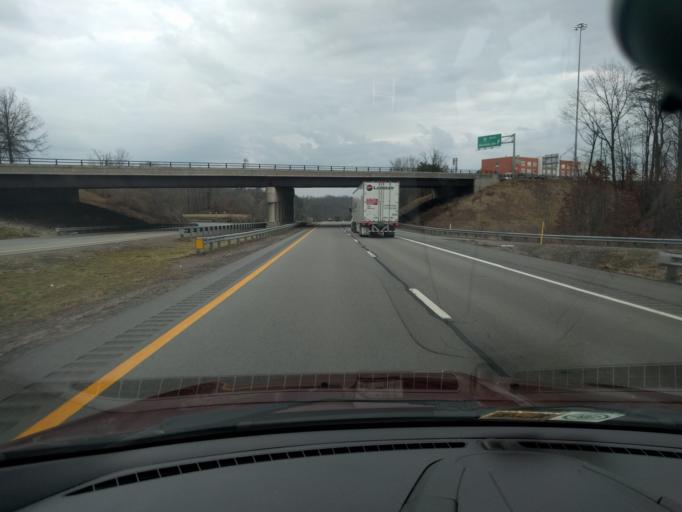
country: US
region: West Virginia
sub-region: Wood County
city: Boaz
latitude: 39.3131
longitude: -81.4786
